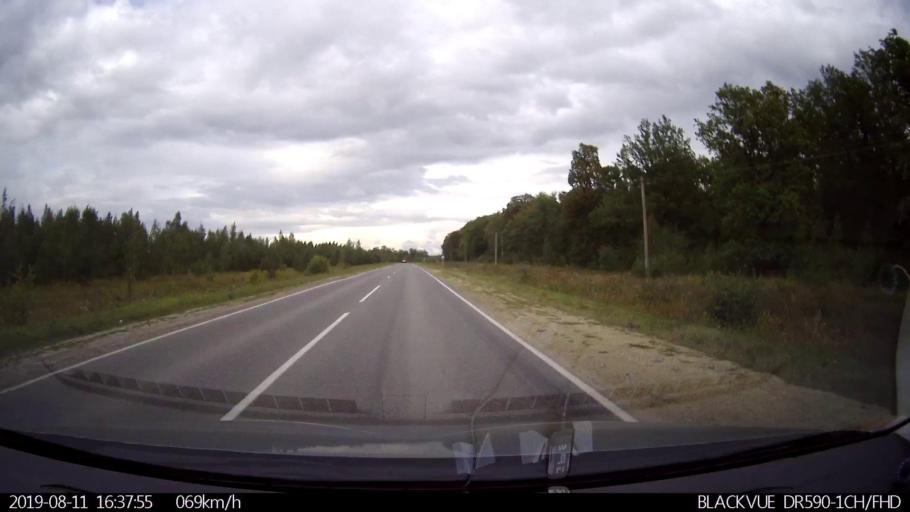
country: RU
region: Ulyanovsk
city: Mayna
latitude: 54.1311
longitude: 47.6188
